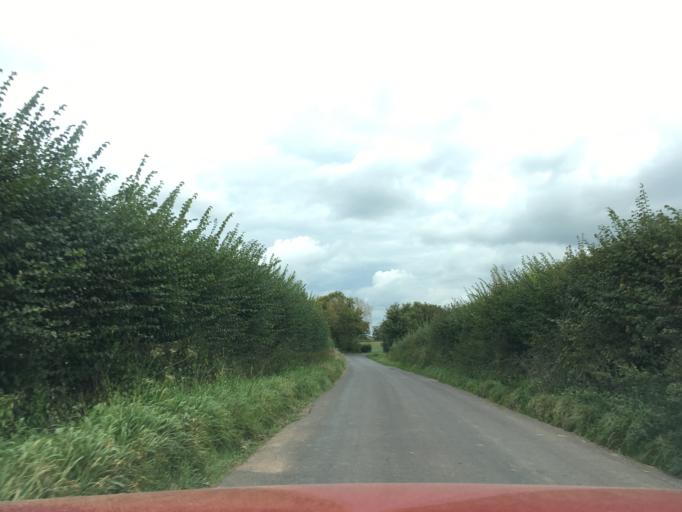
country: GB
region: England
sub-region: Gloucestershire
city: Berkeley
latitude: 51.6783
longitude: -2.4810
